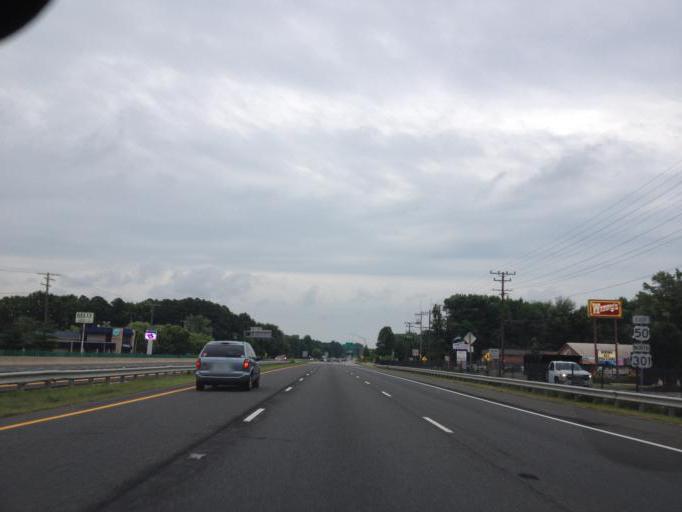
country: US
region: Maryland
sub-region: Anne Arundel County
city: Cape Saint Claire
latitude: 39.0265
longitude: -76.4447
